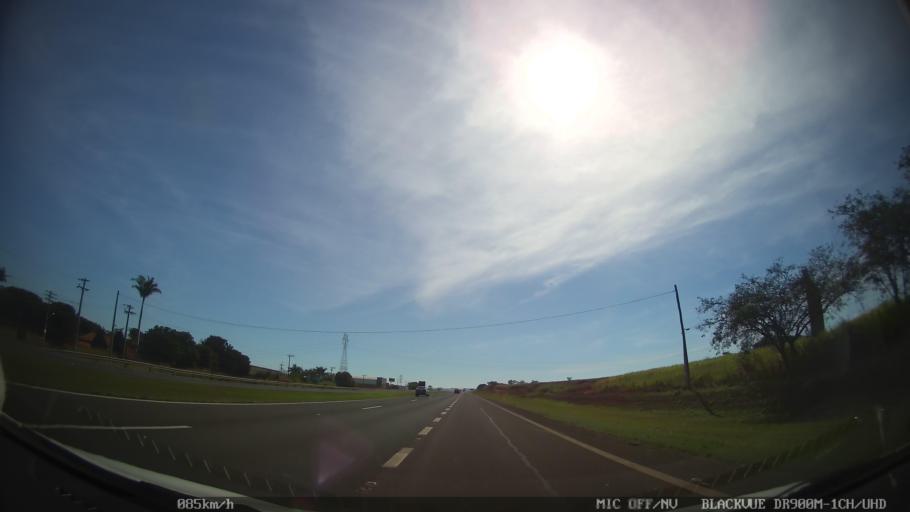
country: BR
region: Sao Paulo
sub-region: Porto Ferreira
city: Porto Ferreira
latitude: -21.8325
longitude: -47.4947
